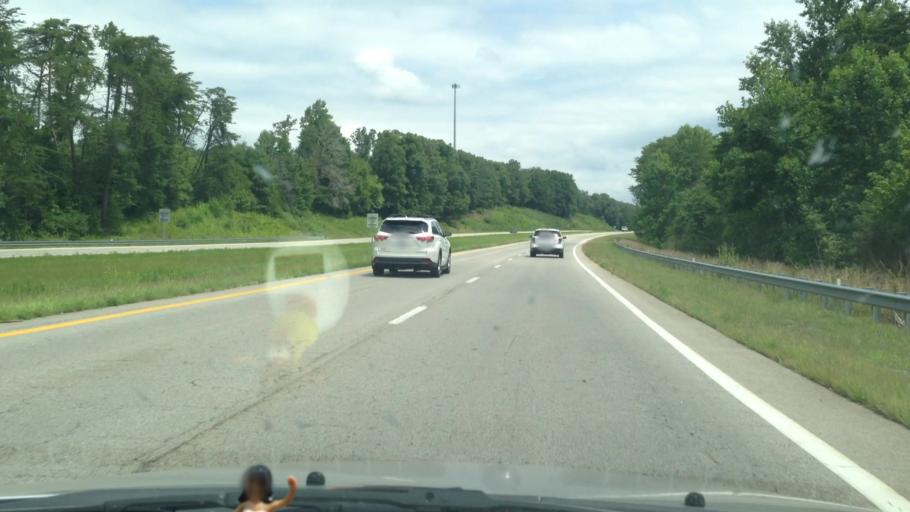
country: US
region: Virginia
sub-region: Pittsylvania County
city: Motley
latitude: 37.1053
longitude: -79.3320
